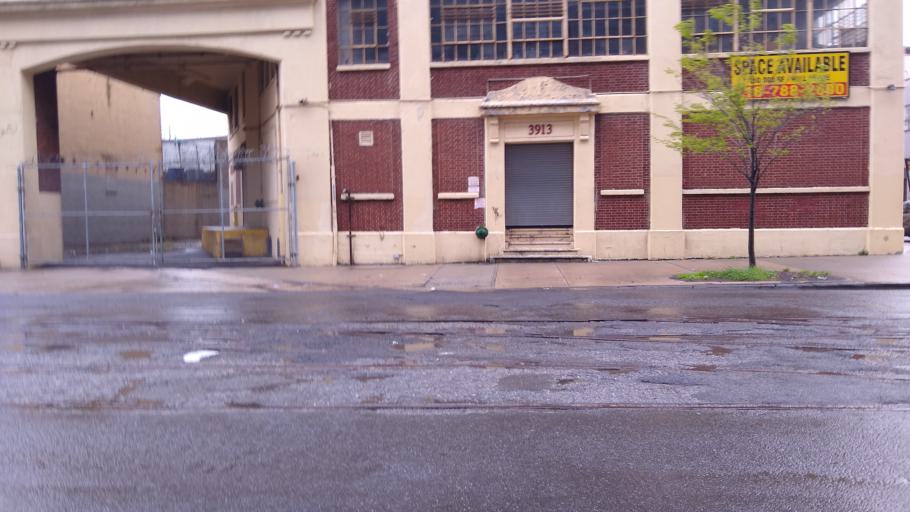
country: US
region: New York
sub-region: Kings County
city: Bensonhurst
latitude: 40.6548
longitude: -74.0110
